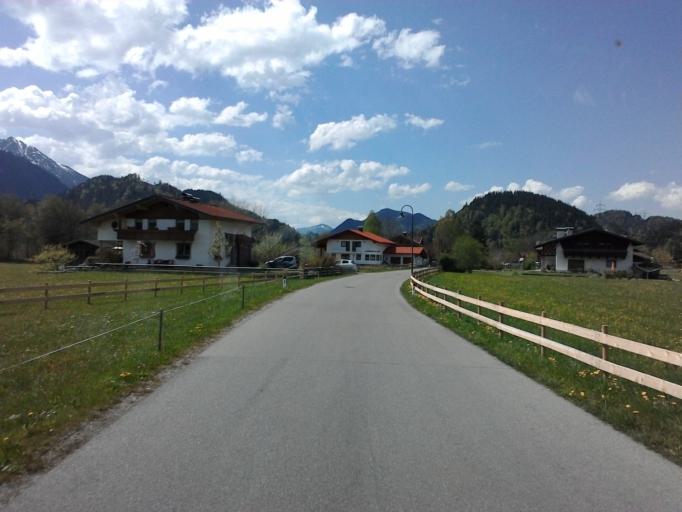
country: AT
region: Tyrol
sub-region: Politischer Bezirk Reutte
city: Musau
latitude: 47.5408
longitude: 10.6791
